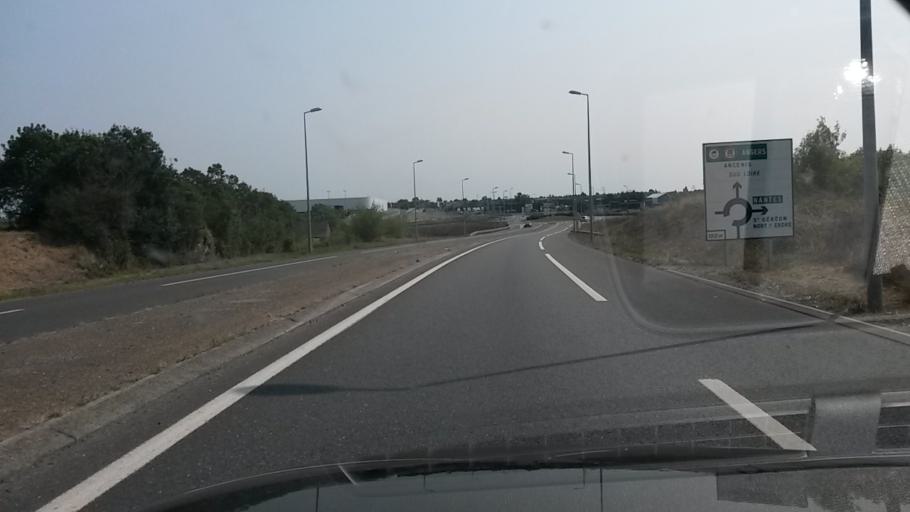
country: FR
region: Pays de la Loire
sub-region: Departement de la Loire-Atlantique
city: Saint-Gereon
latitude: 47.3937
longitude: -1.1891
